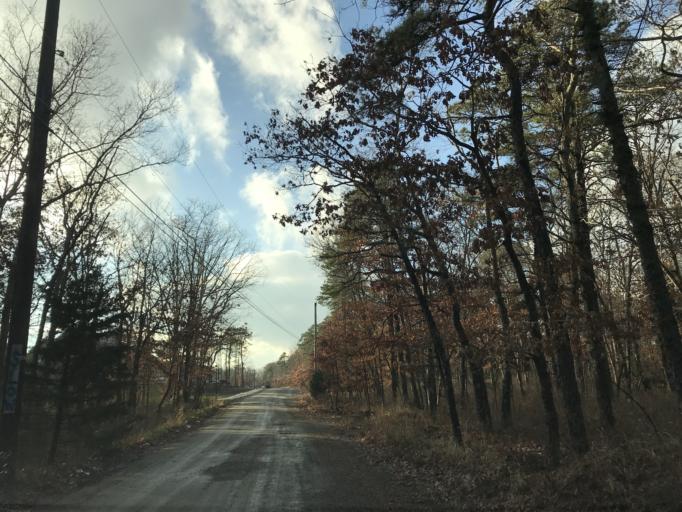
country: US
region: New Jersey
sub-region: Ocean County
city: Waretown
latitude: 39.7920
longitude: -74.2268
